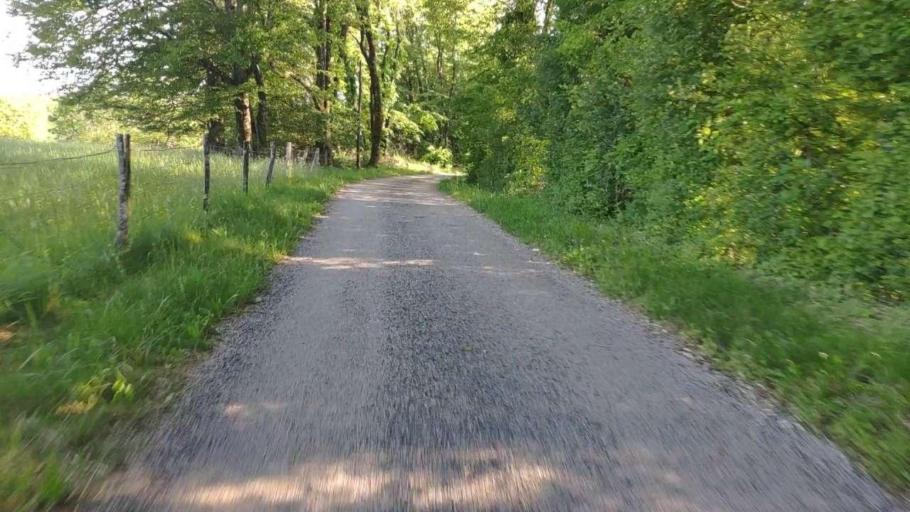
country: FR
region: Franche-Comte
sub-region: Departement du Jura
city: Perrigny
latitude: 46.7277
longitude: 5.6199
